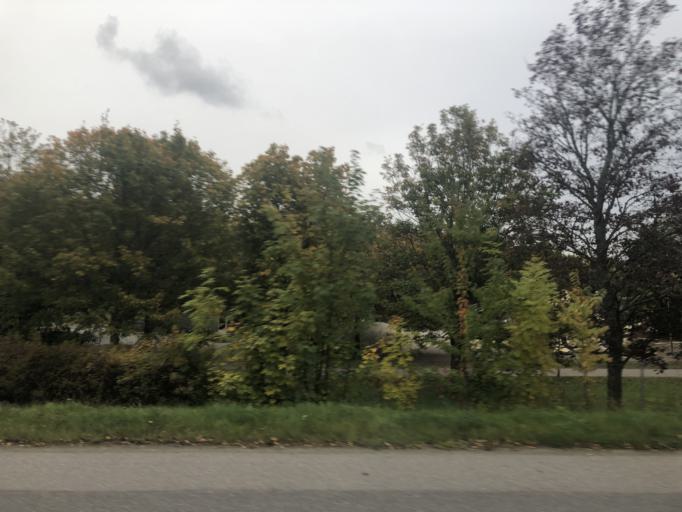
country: SE
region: Stockholm
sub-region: Jarfalla Kommun
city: Jakobsberg
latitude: 59.4167
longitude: 17.8116
